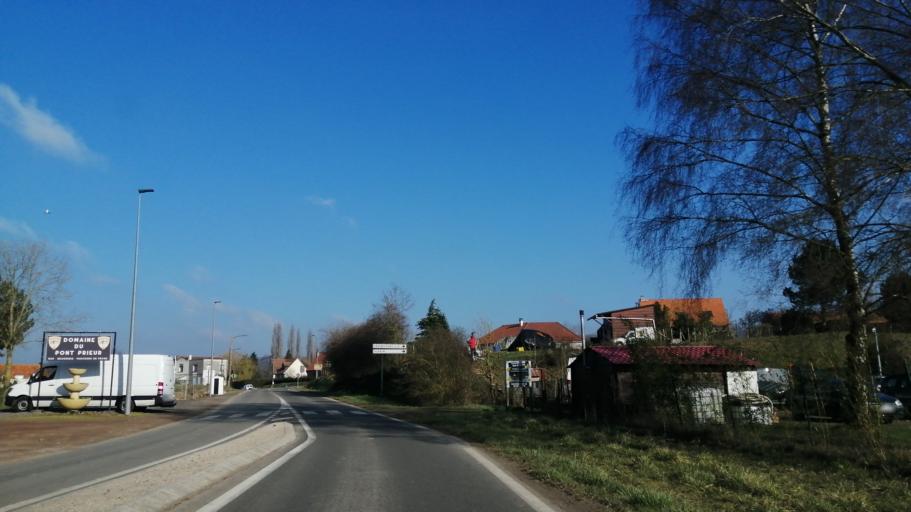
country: FR
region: Nord-Pas-de-Calais
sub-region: Departement du Pas-de-Calais
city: Ranchicourt
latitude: 50.4321
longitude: 2.5605
